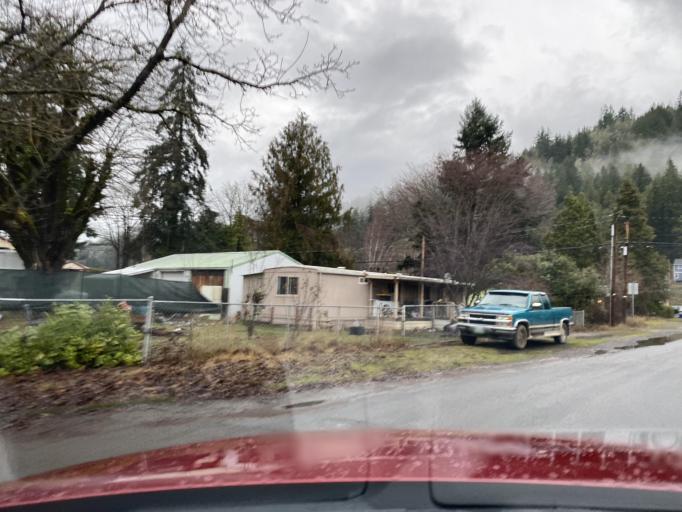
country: US
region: Oregon
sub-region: Lane County
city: Oakridge
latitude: 43.7472
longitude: -122.4662
